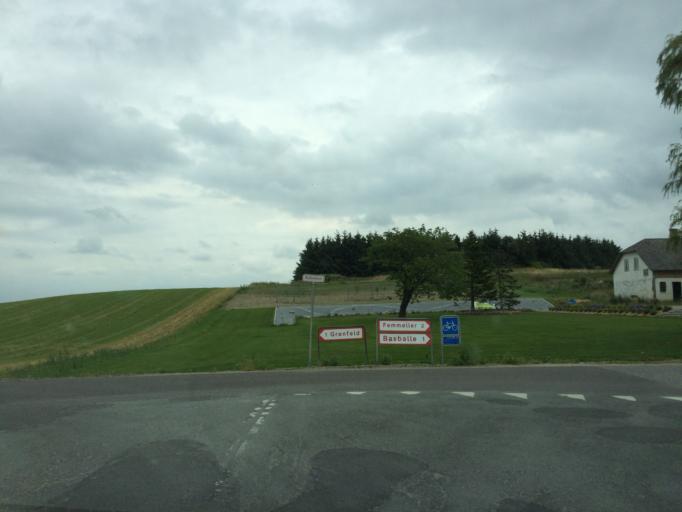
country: DK
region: Central Jutland
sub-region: Syddjurs Kommune
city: Ronde
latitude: 56.2436
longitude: 10.5483
